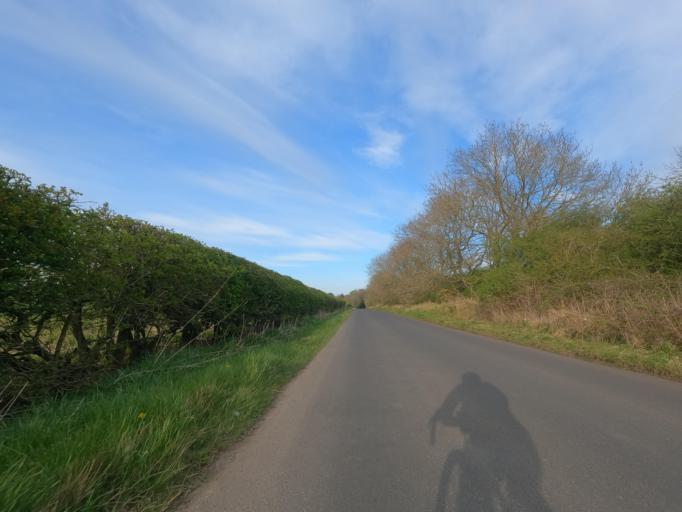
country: GB
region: England
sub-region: Newcastle upon Tyne
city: Hazlerigg
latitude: 55.0688
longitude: -1.6260
